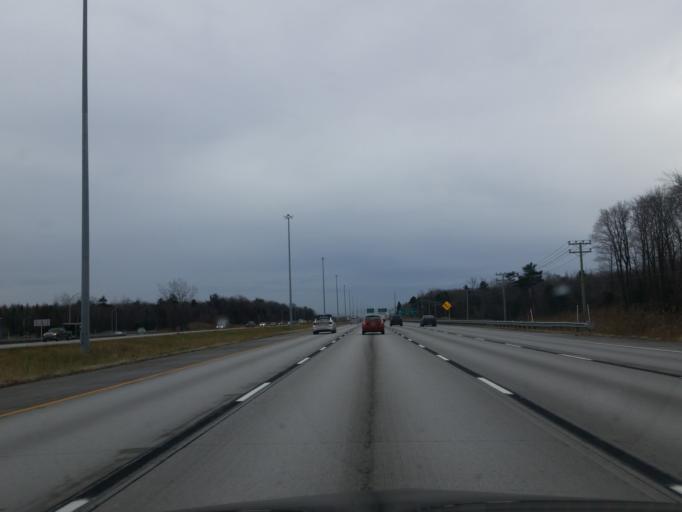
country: CA
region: Quebec
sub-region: Laurentides
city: Blainville
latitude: 45.6604
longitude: -73.8896
